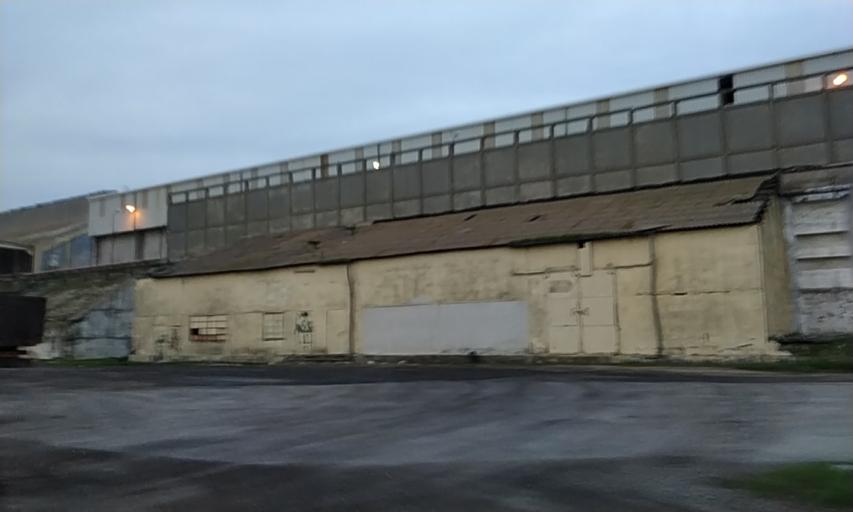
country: PT
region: Setubal
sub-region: Setubal
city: Setubal
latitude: 38.4998
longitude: -8.8397
